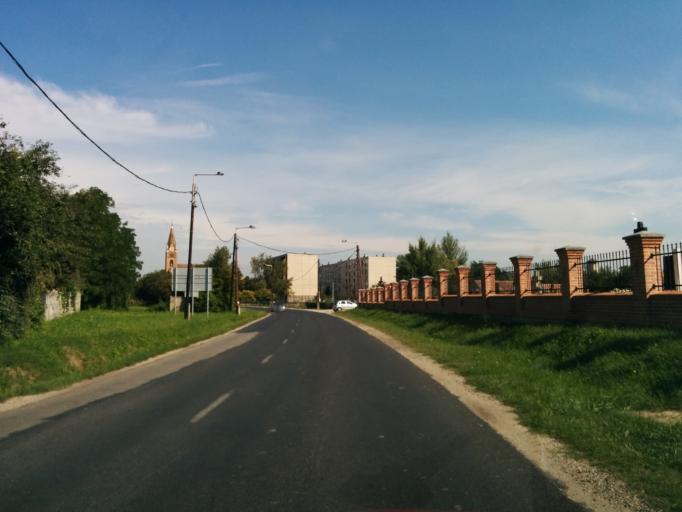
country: HU
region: Gyor-Moson-Sopron
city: Fertod
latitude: 47.6161
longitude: 16.8885
